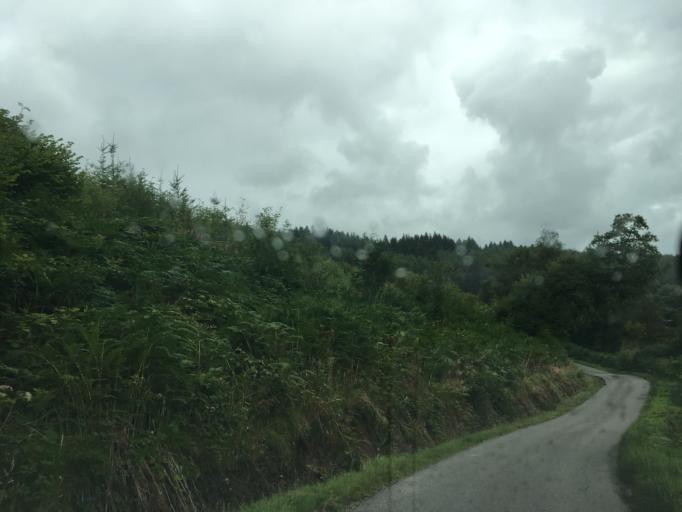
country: GB
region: Scotland
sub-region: Argyll and Bute
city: Oban
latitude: 56.2779
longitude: -5.3617
